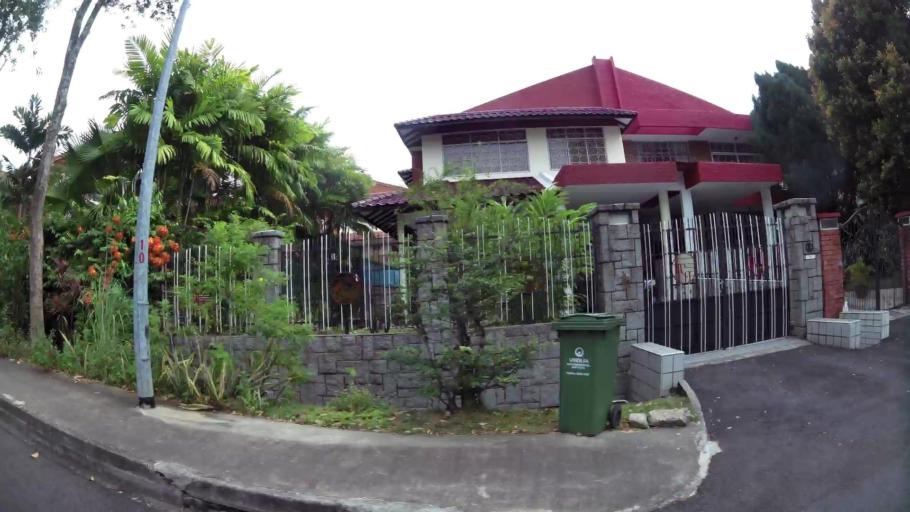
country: SG
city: Singapore
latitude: 1.3327
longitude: 103.7992
